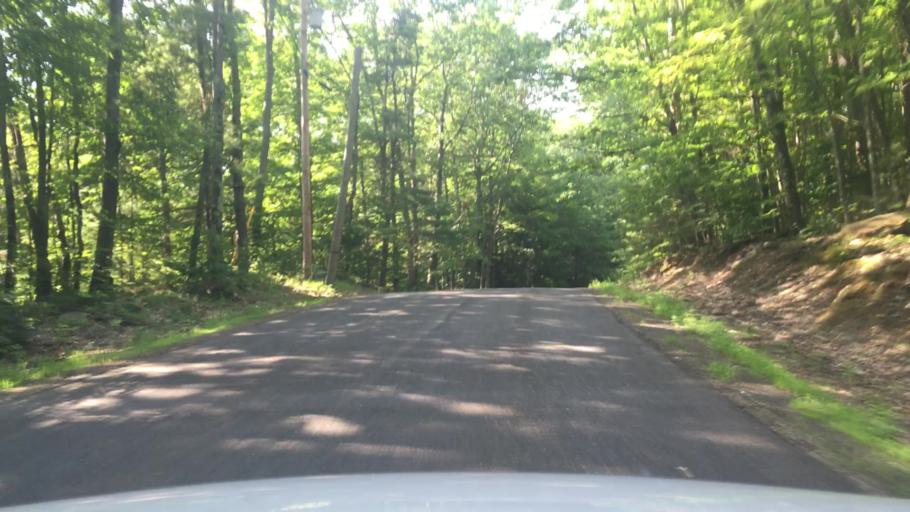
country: US
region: Maine
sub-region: Androscoggin County
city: Greene
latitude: 44.2372
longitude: -70.1056
